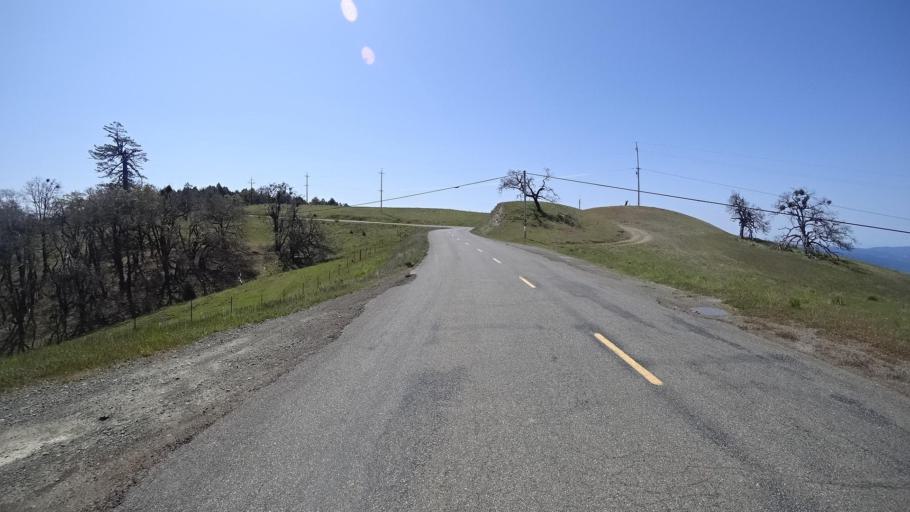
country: US
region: California
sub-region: Humboldt County
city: Redway
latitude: 40.0981
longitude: -123.6832
